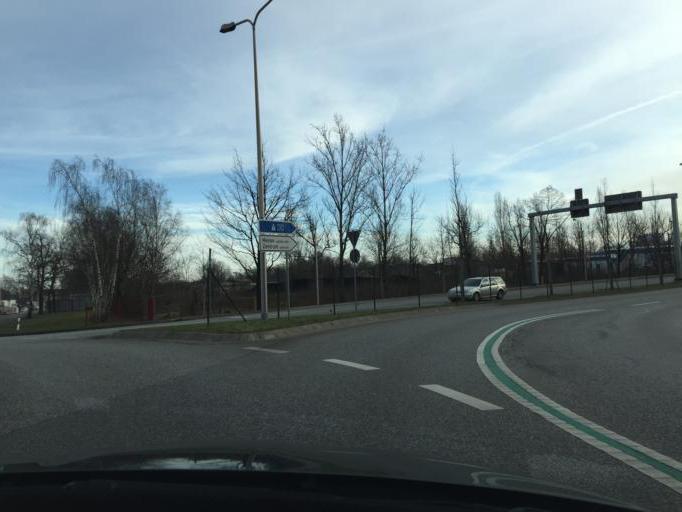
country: DE
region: Brandenburg
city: Cottbus
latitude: 51.7681
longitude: 14.3574
